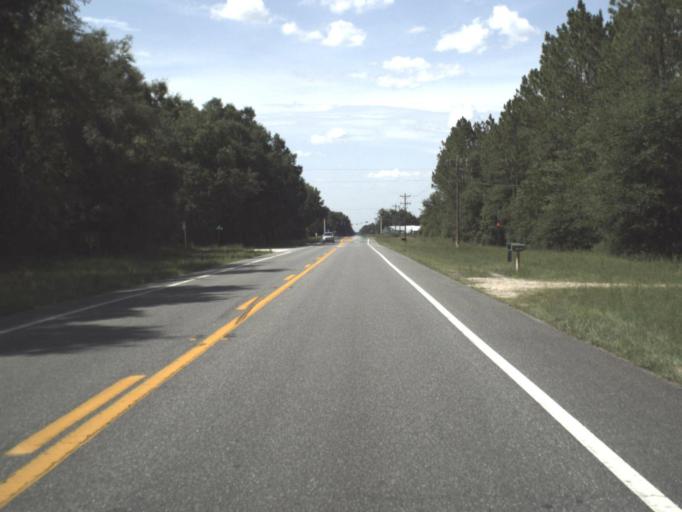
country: US
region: Florida
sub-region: Alachua County
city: High Springs
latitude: 29.8056
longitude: -82.7412
